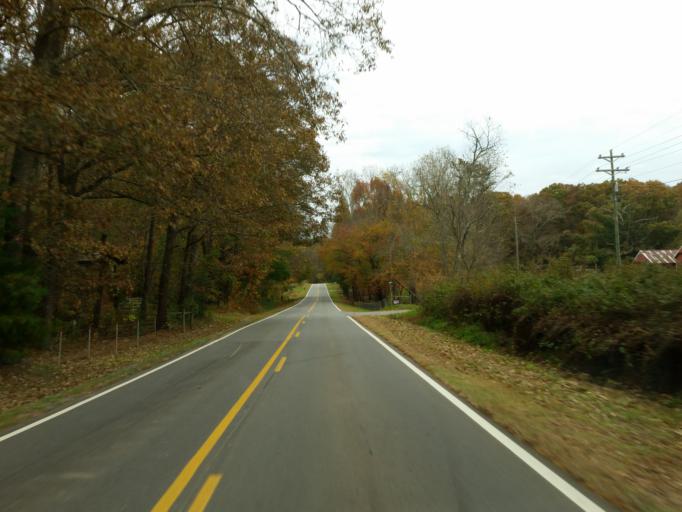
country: US
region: Georgia
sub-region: Gilmer County
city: Ellijay
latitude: 34.6519
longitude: -84.3844
